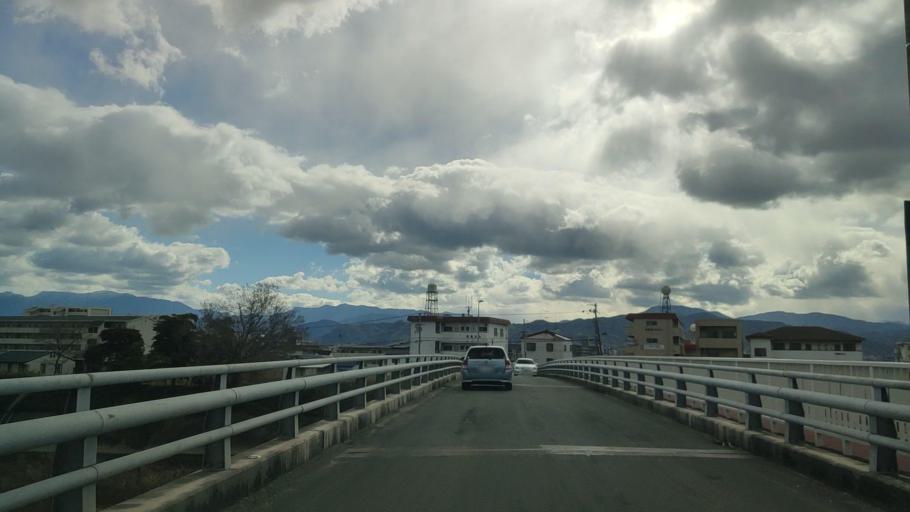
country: JP
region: Ehime
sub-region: Shikoku-chuo Shi
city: Matsuyama
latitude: 33.8156
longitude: 132.7522
